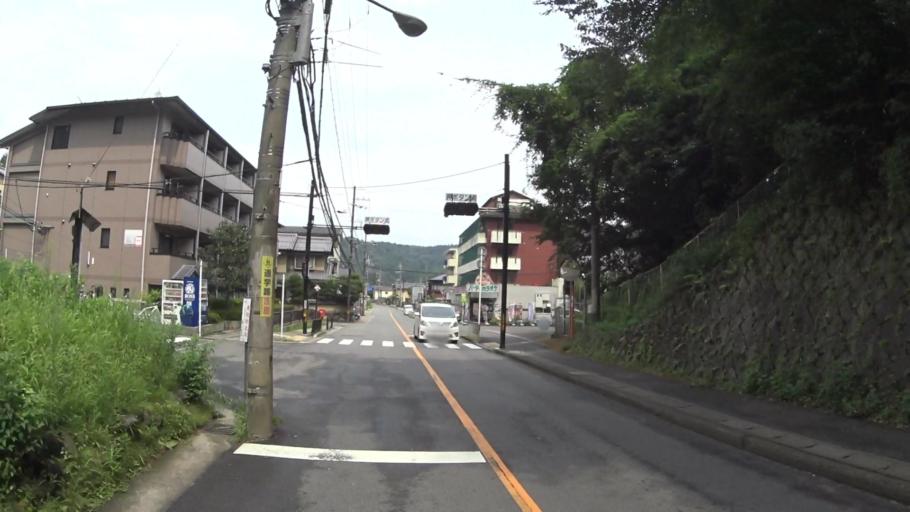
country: JP
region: Kyoto
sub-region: Kyoto-shi
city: Kamigyo-ku
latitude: 35.0737
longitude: 135.7601
